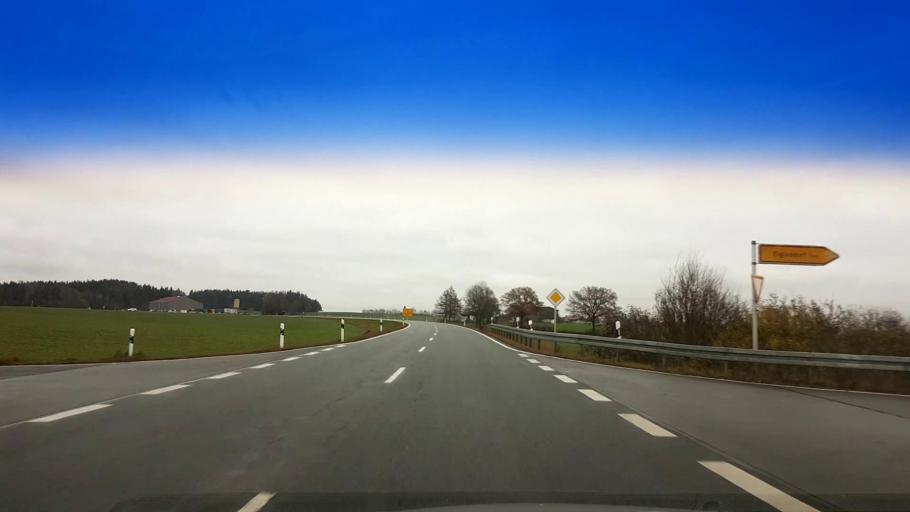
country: DE
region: Bavaria
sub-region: Upper Palatinate
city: Berg
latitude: 49.8393
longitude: 12.1384
